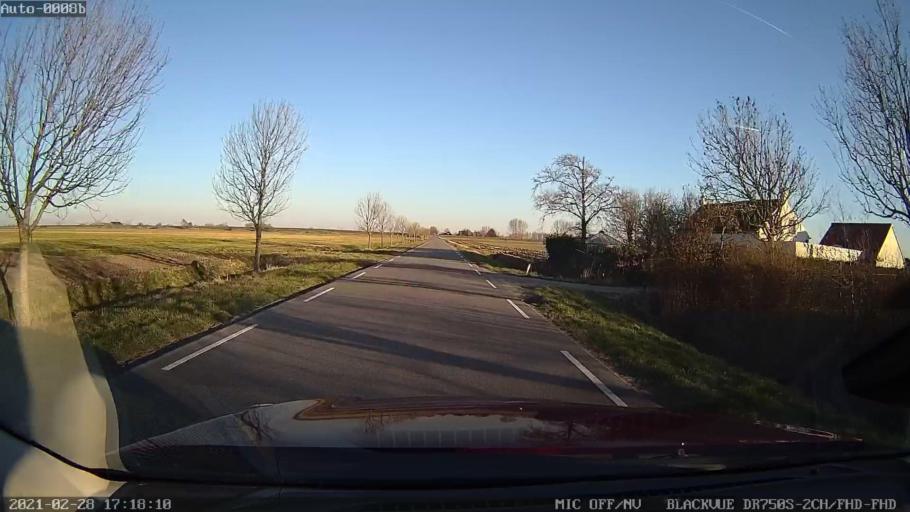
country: NL
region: South Holland
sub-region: Gemeente Goeree-Overflakkee
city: Ouddorp
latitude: 51.7044
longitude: 3.9535
